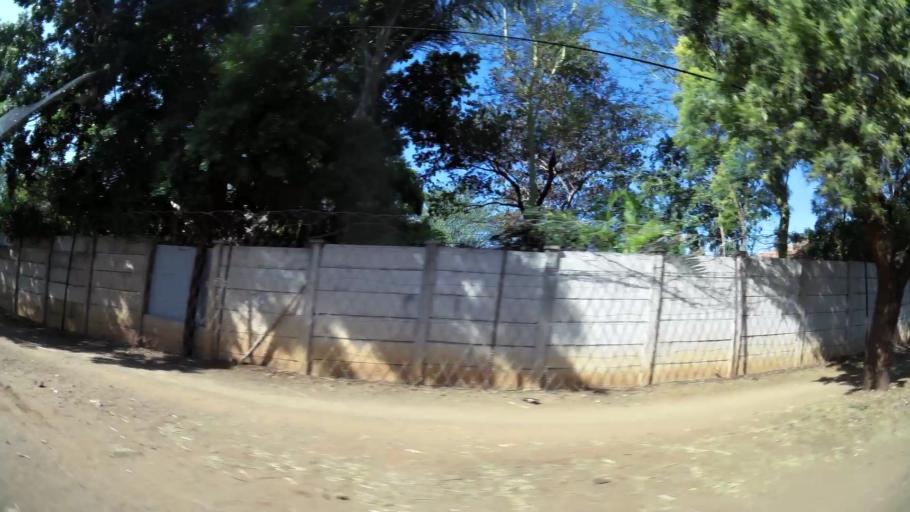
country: ZA
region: Gauteng
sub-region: City of Tshwane Metropolitan Municipality
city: Pretoria
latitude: -25.6719
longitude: 28.2548
